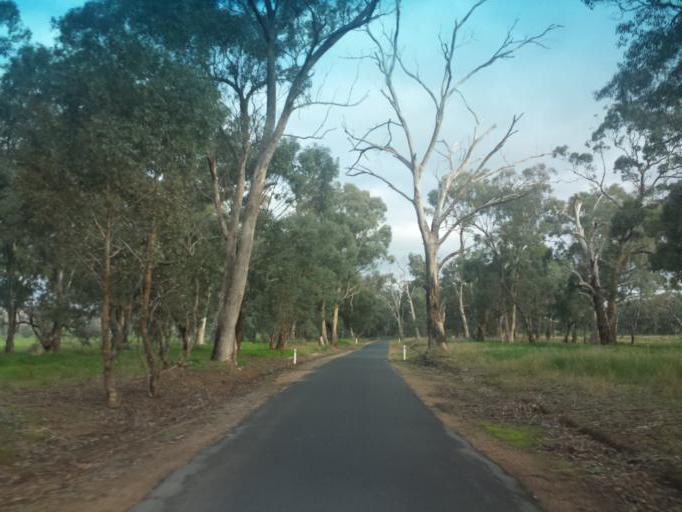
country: AU
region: Victoria
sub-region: Murrindindi
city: Kinglake West
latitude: -36.9196
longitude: 145.2255
